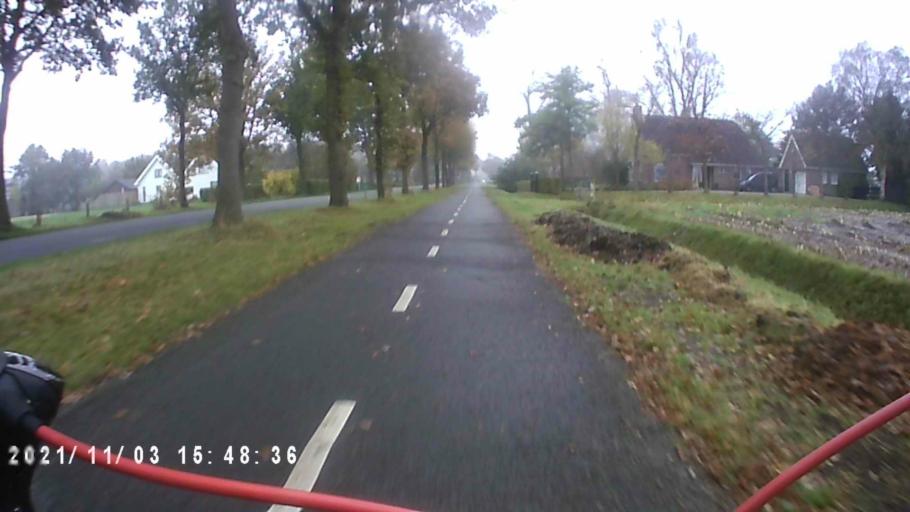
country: NL
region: Groningen
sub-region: Gemeente Leek
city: Leek
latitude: 53.0869
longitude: 6.3389
